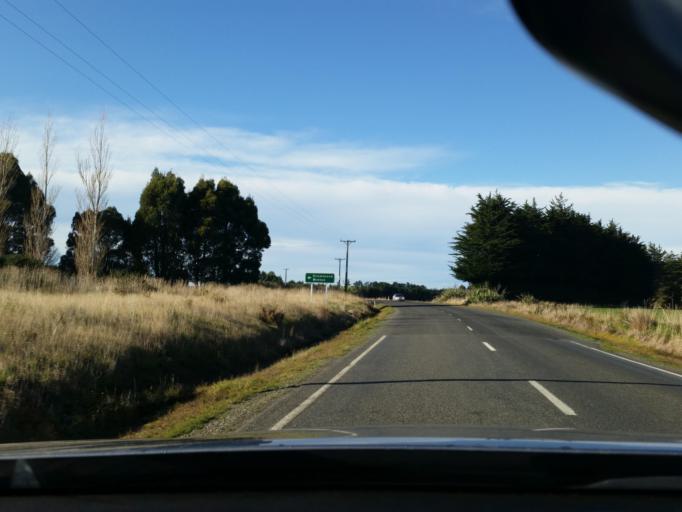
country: NZ
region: Southland
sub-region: Southland District
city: Riverton
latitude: -46.1690
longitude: 168.0879
